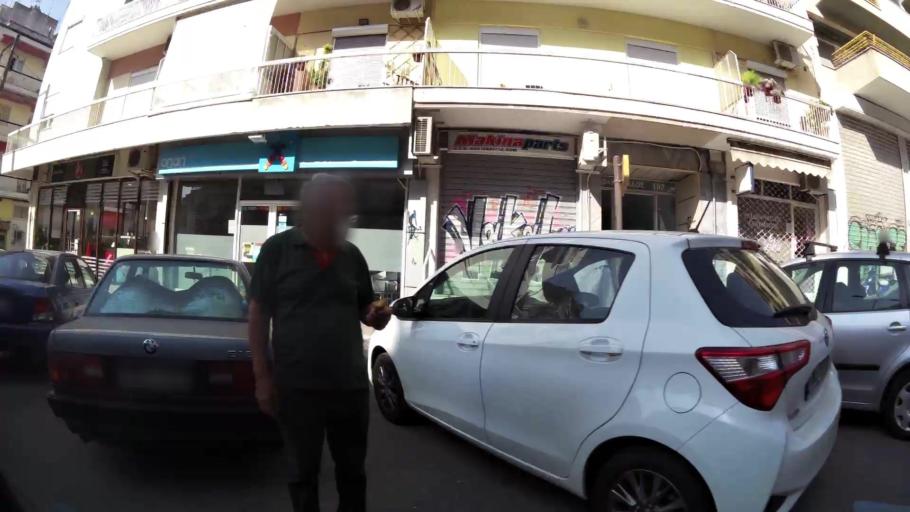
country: GR
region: Central Macedonia
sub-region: Nomos Thessalonikis
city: Agios Pavlos
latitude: 40.6383
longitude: 22.9529
